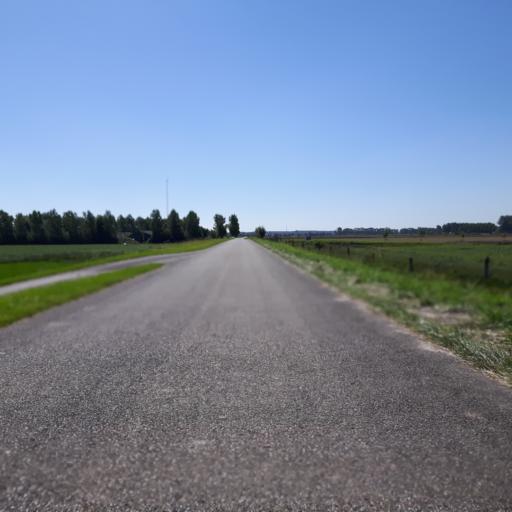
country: NL
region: Zeeland
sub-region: Gemeente Noord-Beveland
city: Kamperland
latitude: 51.5857
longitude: 3.7890
